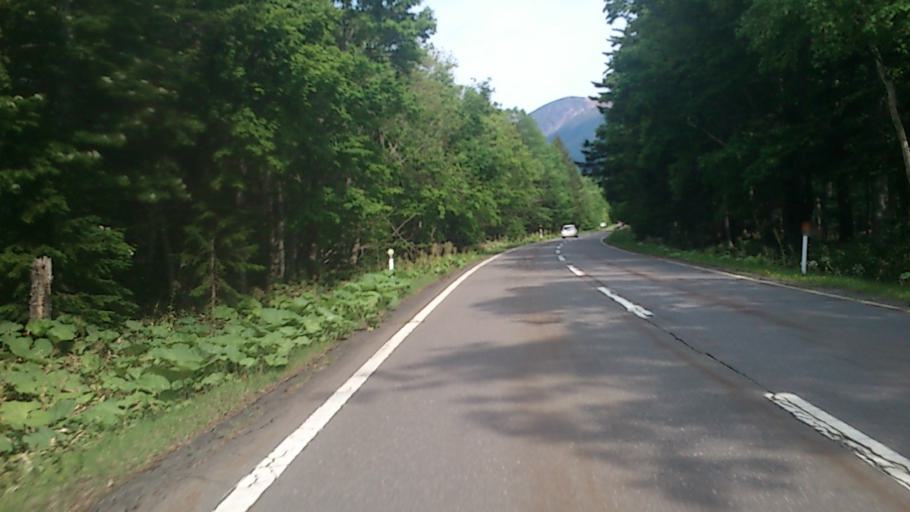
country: JP
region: Hokkaido
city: Kitami
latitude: 43.4058
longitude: 143.9580
